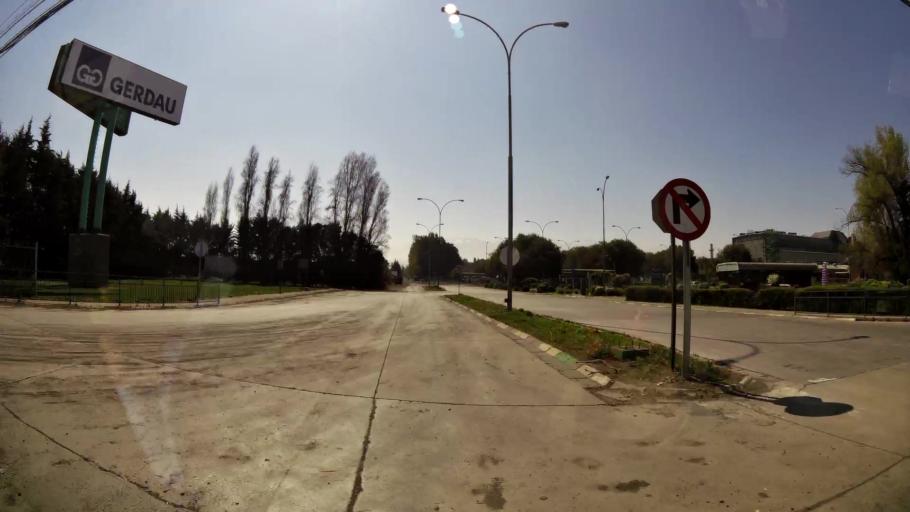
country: CL
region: Santiago Metropolitan
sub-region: Provincia de Chacabuco
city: Chicureo Abajo
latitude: -33.2953
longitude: -70.7316
